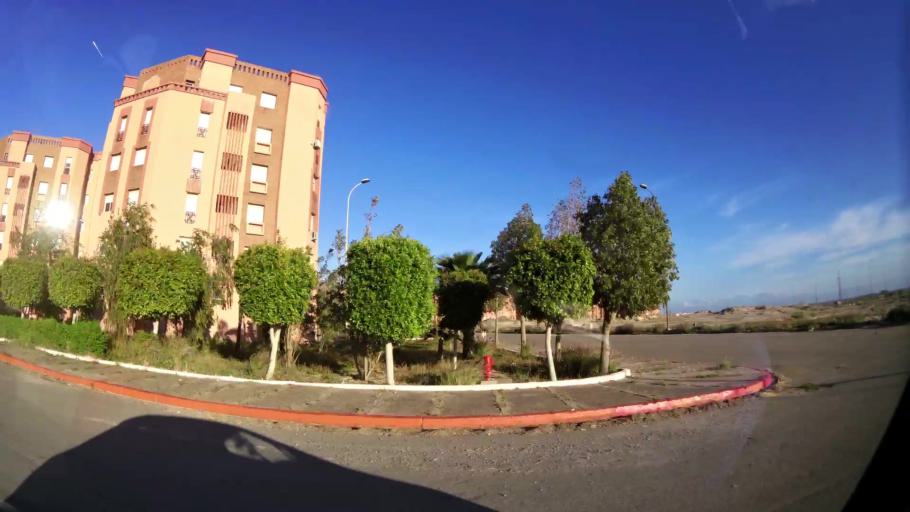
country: MA
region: Marrakech-Tensift-Al Haouz
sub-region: Marrakech
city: Marrakesh
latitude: 31.7482
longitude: -8.1312
